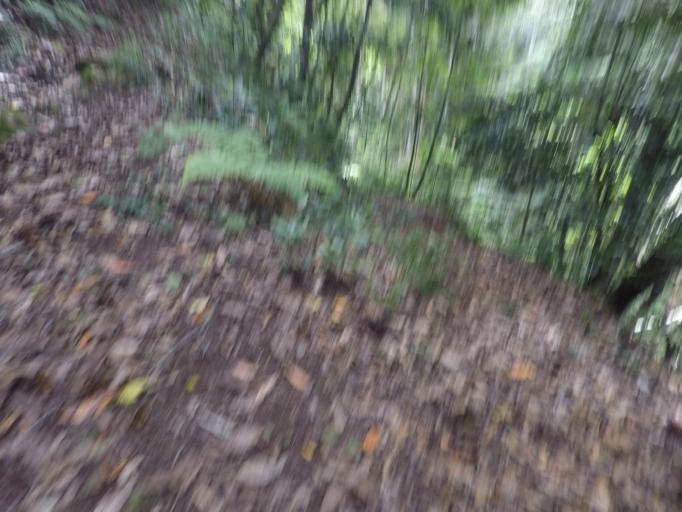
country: PT
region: Madeira
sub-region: Porto Moniz
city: Porto Moniz
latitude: 32.8342
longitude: -17.1399
